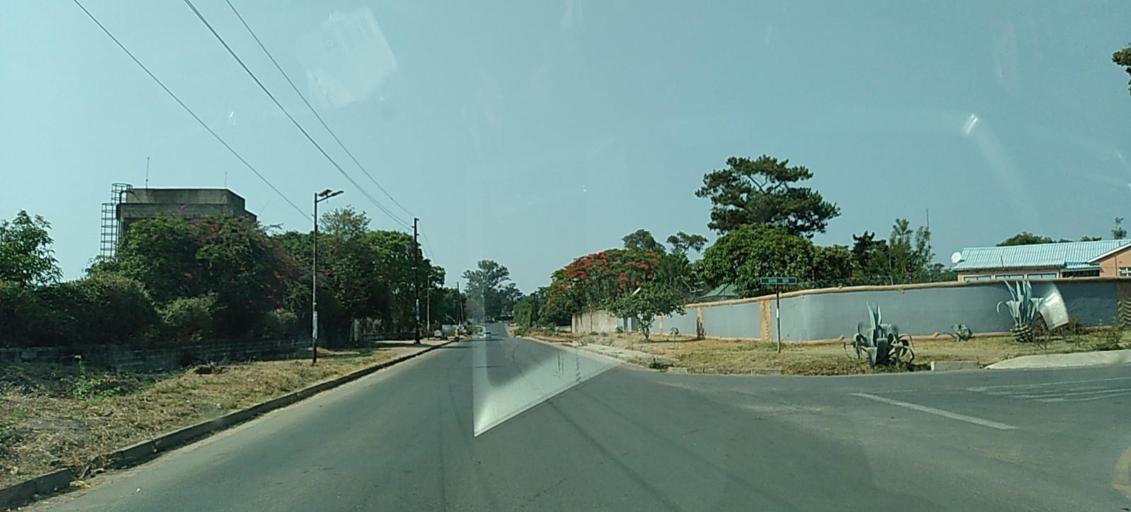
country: ZM
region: Copperbelt
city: Chingola
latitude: -12.5478
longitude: 27.8709
